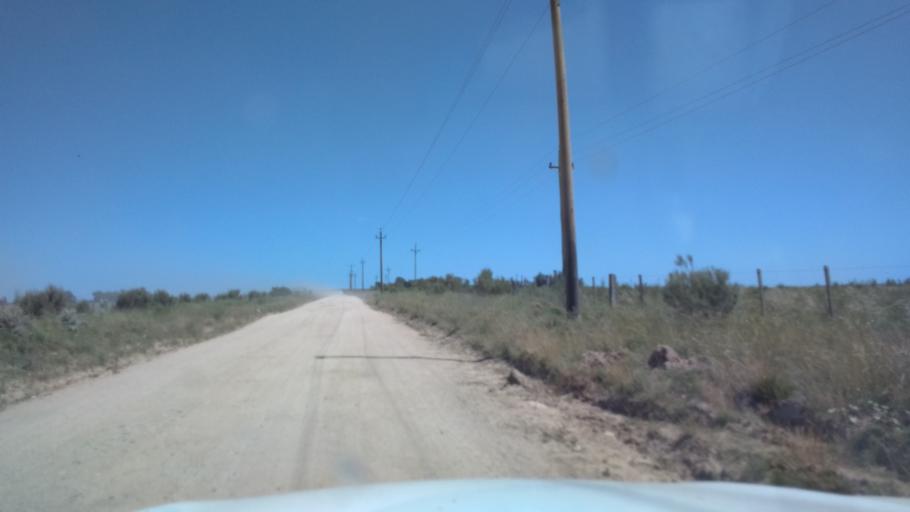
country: UY
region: Florida
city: Casupa
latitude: -34.0528
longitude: -55.8940
